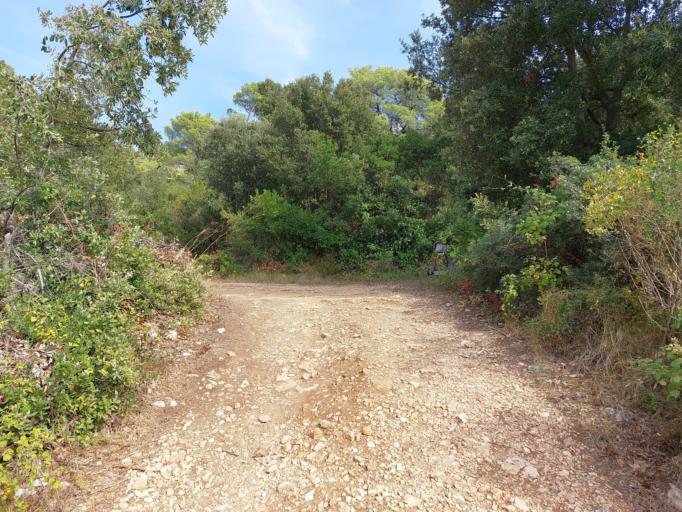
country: HR
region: Dubrovacko-Neretvanska
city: Smokvica
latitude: 42.7487
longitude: 16.8374
